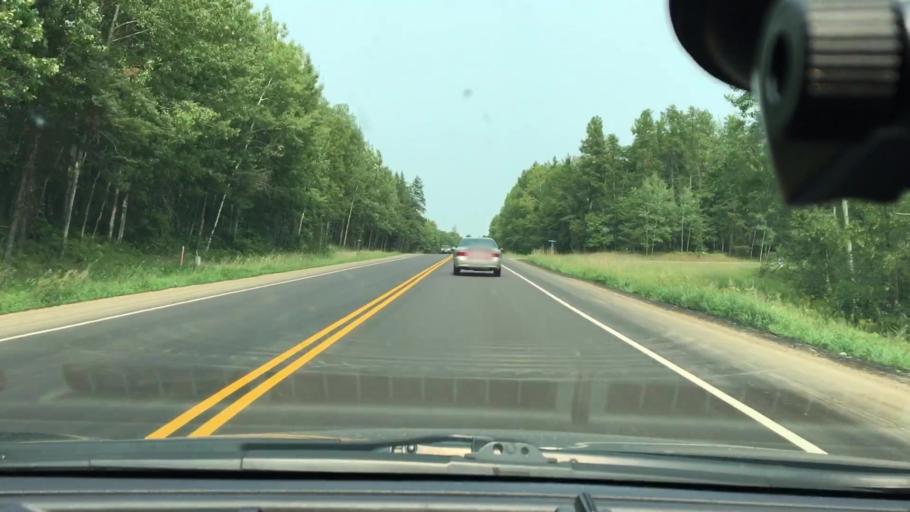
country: US
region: Minnesota
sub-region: Crow Wing County
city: Nisswa
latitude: 46.5249
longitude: -94.2709
